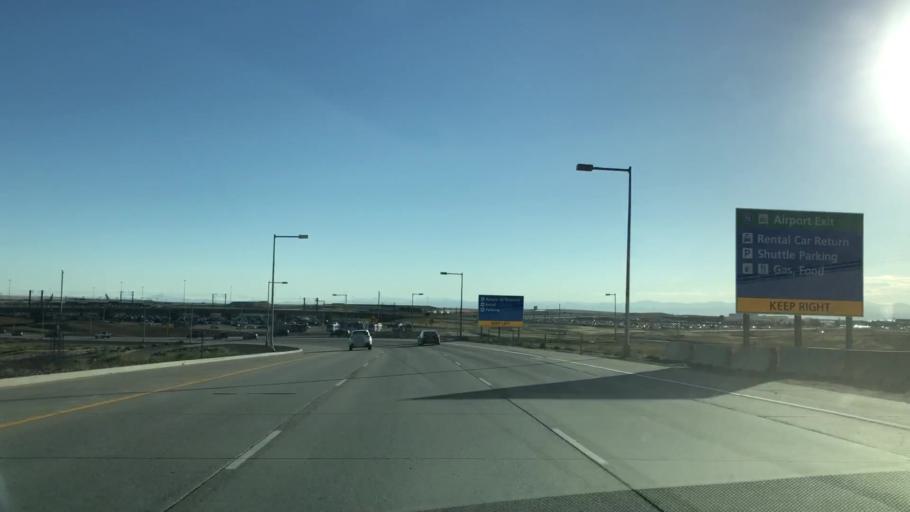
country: US
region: Colorado
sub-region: Weld County
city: Lochbuie
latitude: 39.8418
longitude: -104.6749
